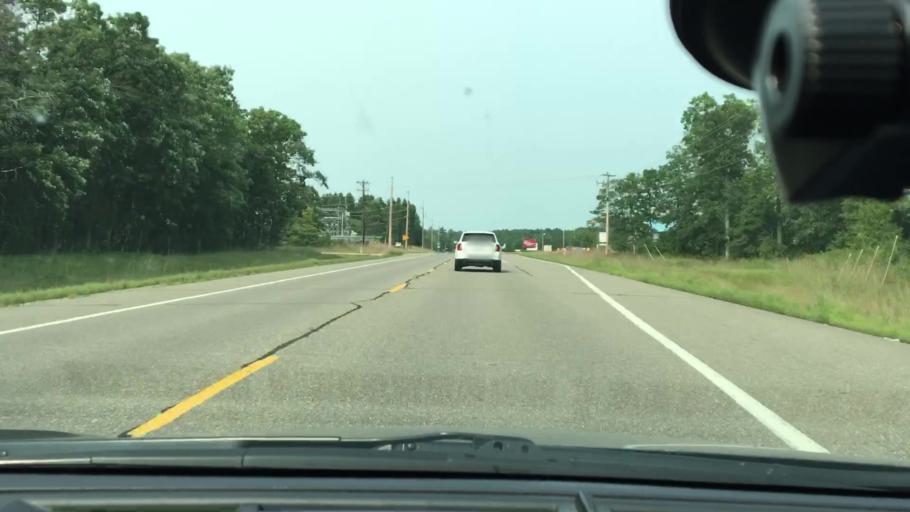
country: US
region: Minnesota
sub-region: Crow Wing County
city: Cross Lake
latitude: 46.6125
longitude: -94.1317
